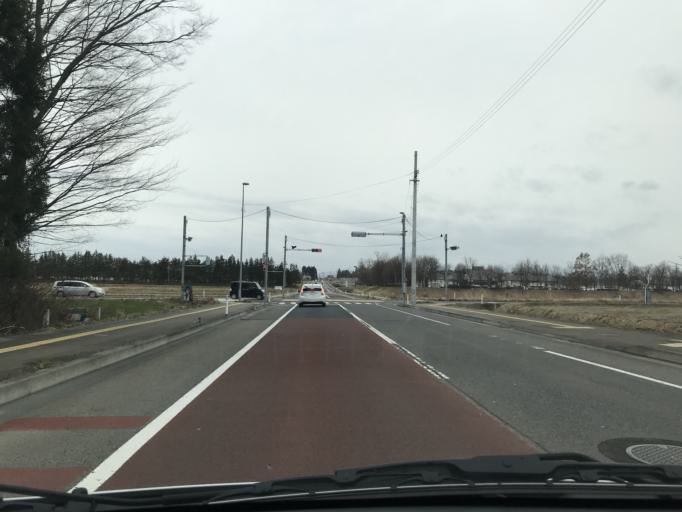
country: JP
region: Iwate
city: Hanamaki
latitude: 39.3577
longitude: 141.1088
